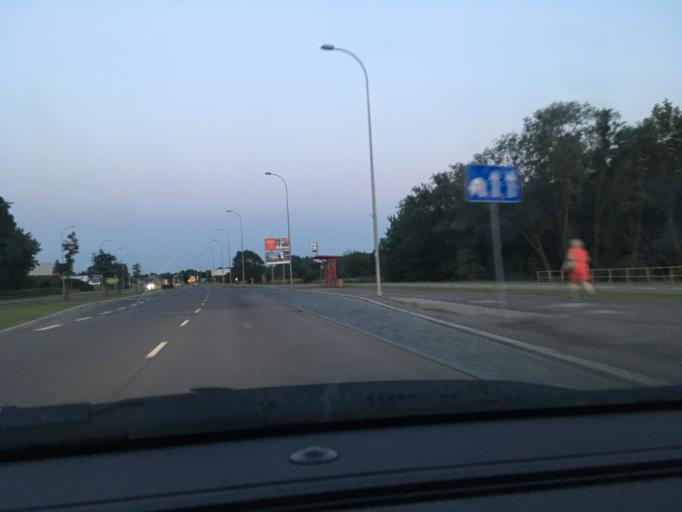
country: PL
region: Podlasie
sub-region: Bialystok
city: Bialystok
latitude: 53.1233
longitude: 23.1869
